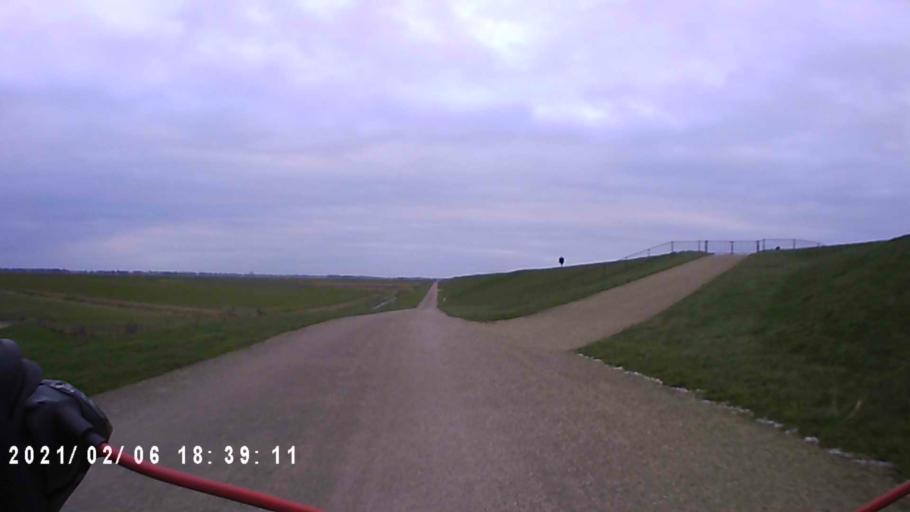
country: NL
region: Groningen
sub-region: Gemeente Bedum
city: Bedum
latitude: 53.4422
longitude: 6.6131
